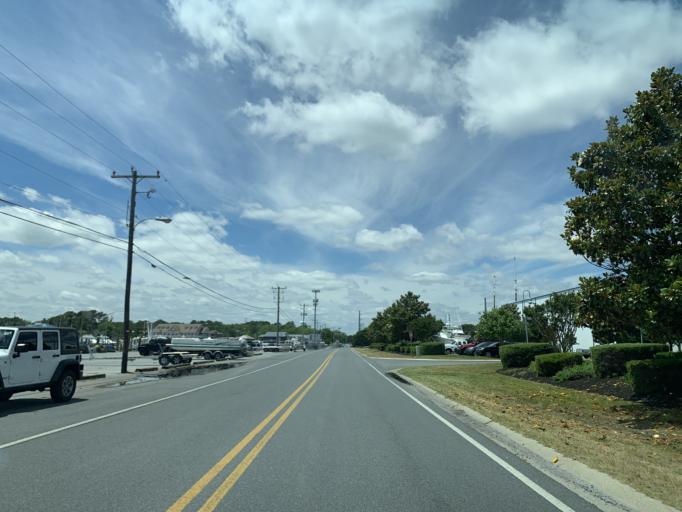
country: US
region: Maryland
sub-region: Worcester County
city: West Ocean City
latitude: 38.3279
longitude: -75.1042
